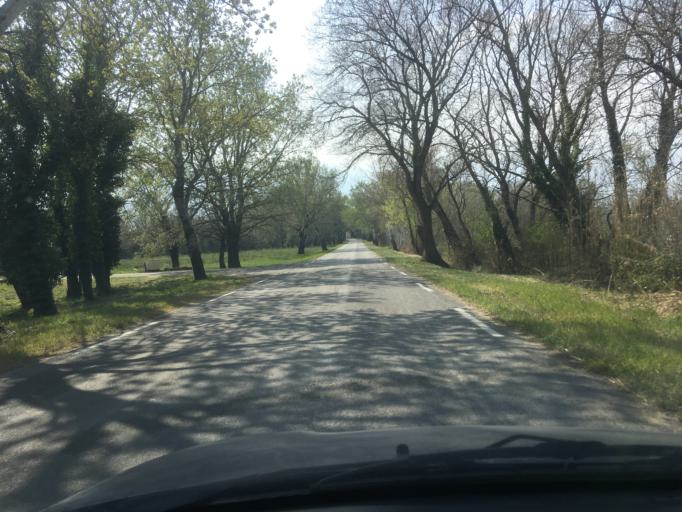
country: FR
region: Provence-Alpes-Cote d'Azur
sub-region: Departement du Vaucluse
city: Loriol-du-Comtat
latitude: 44.0990
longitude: 4.9982
